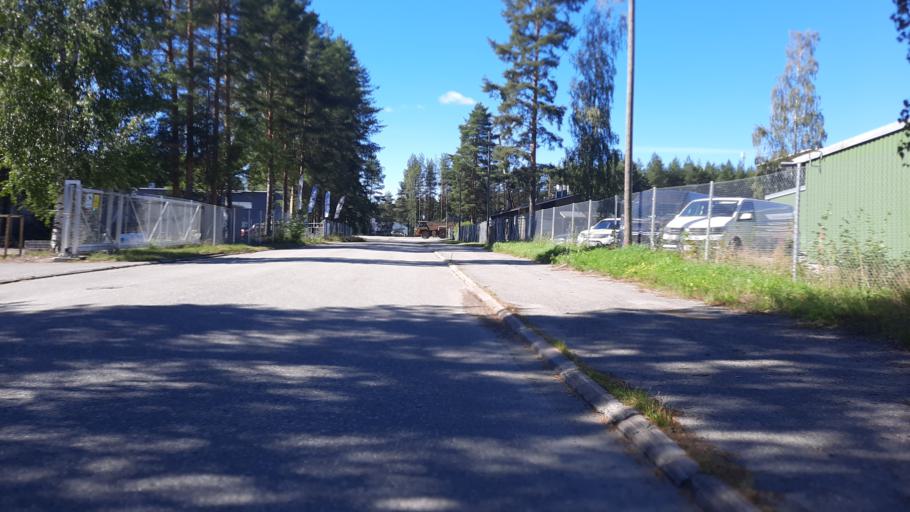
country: FI
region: North Karelia
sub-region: Joensuu
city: Joensuu
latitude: 62.6199
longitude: 29.7422
